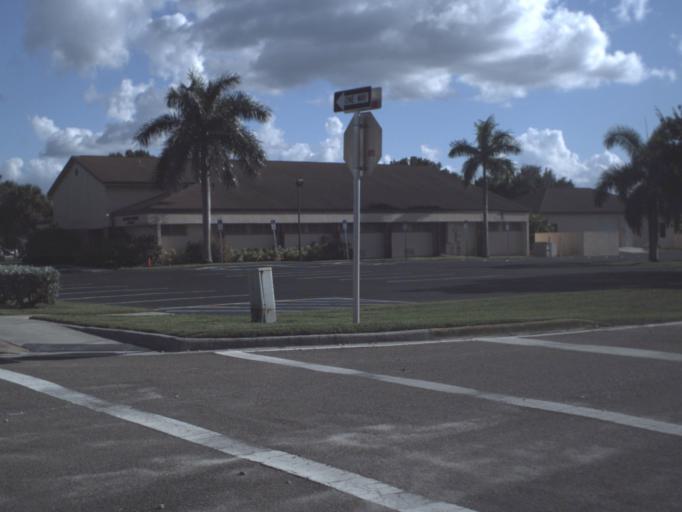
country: US
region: Florida
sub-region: Charlotte County
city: Punta Gorda
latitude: 26.9314
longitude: -82.0494
